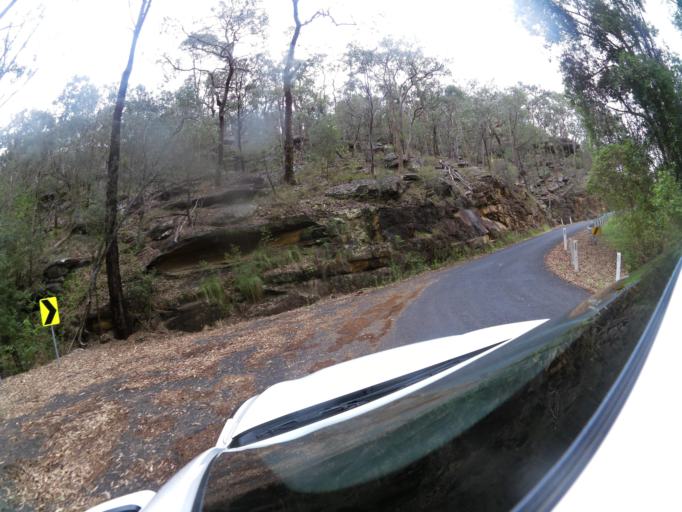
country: AU
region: New South Wales
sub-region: Hawkesbury
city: Pitt Town
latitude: -33.4317
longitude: 150.9312
